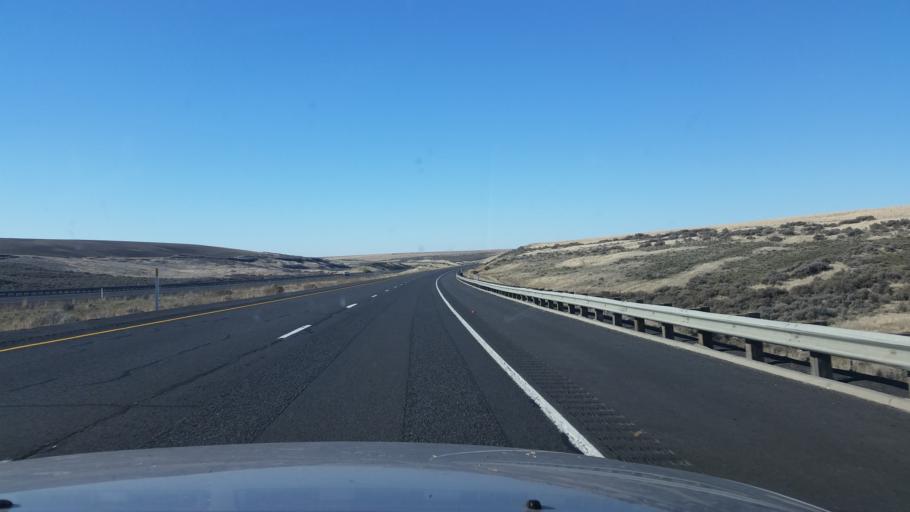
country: US
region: Washington
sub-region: Adams County
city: Ritzville
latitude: 47.1108
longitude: -118.5525
